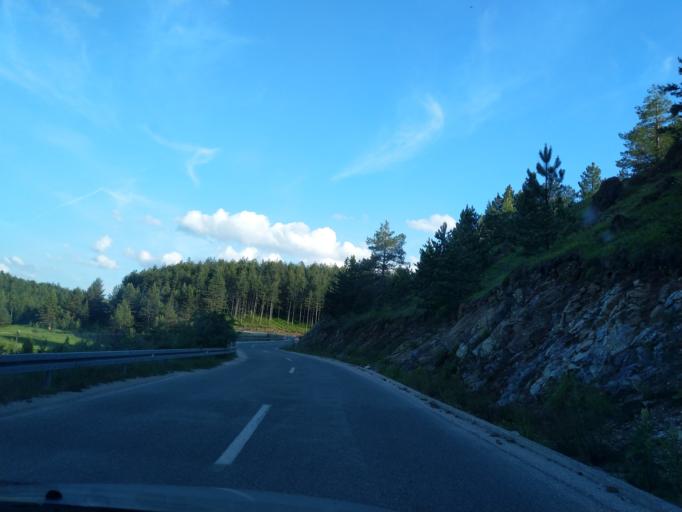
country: RS
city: Zlatibor
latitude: 43.6918
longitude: 19.6620
